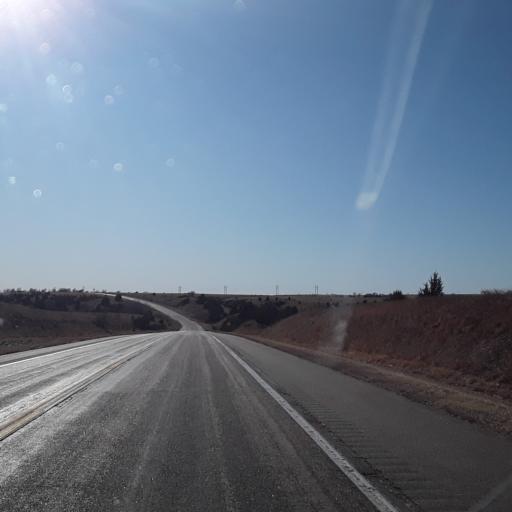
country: US
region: Nebraska
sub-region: Frontier County
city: Stockville
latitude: 40.5468
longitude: -100.6426
